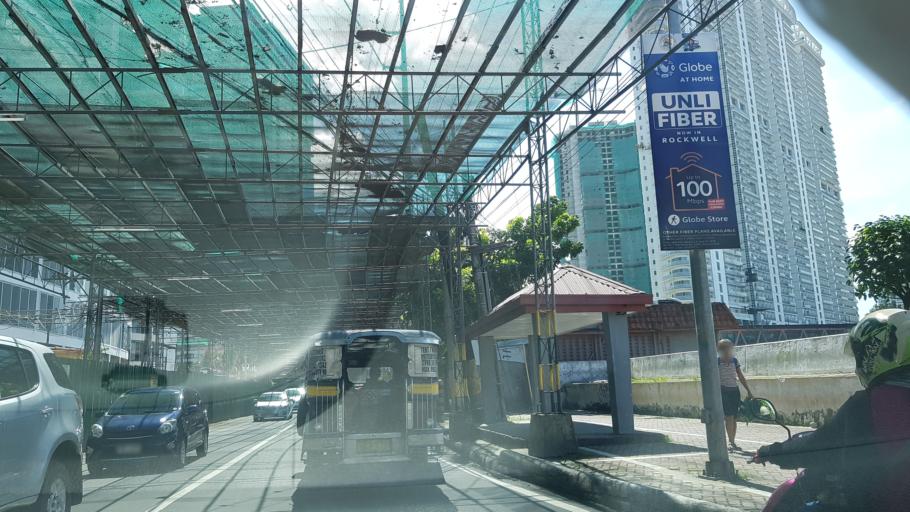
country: PH
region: Metro Manila
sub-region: Mandaluyong
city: Mandaluyong City
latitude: 14.5674
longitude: 121.0392
